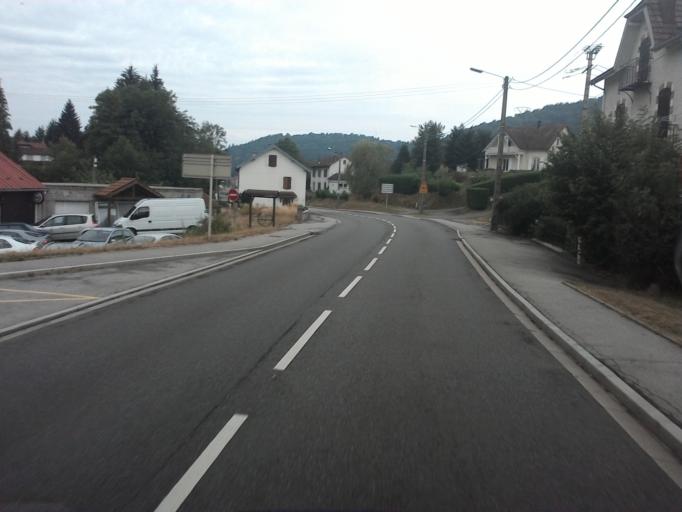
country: FR
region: Lorraine
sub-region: Departement des Vosges
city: Fresse-sur-Moselle
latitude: 47.8728
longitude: 6.7898
